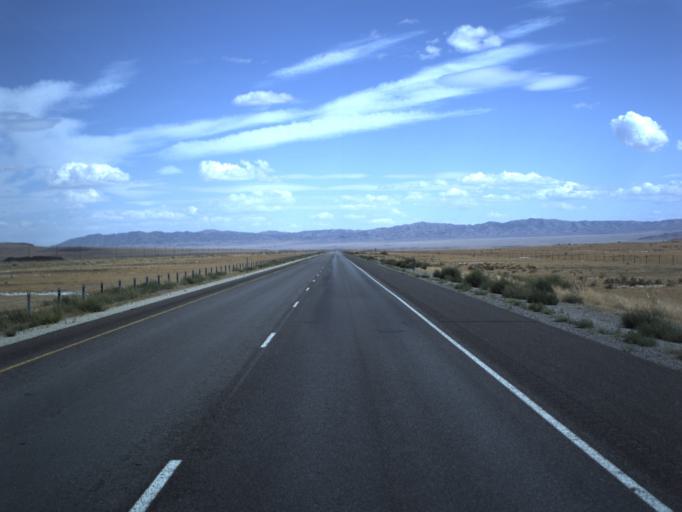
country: US
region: Utah
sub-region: Tooele County
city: Grantsville
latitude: 40.7259
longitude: -113.2094
